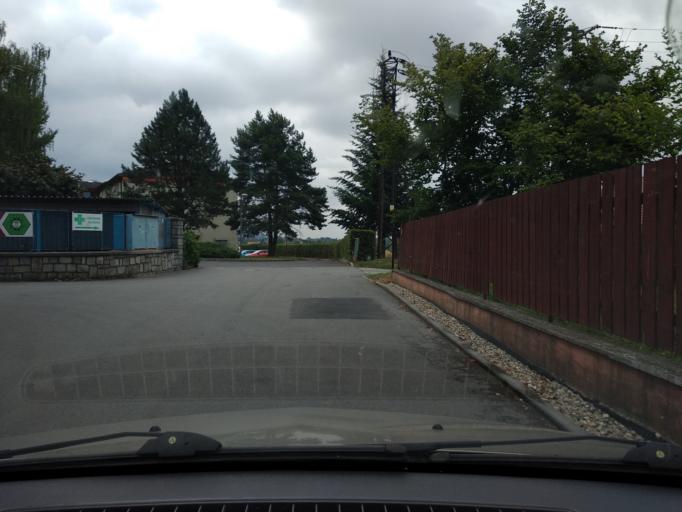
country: CZ
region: Olomoucky
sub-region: Okres Sumperk
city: Bludov
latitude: 49.9400
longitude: 16.9250
